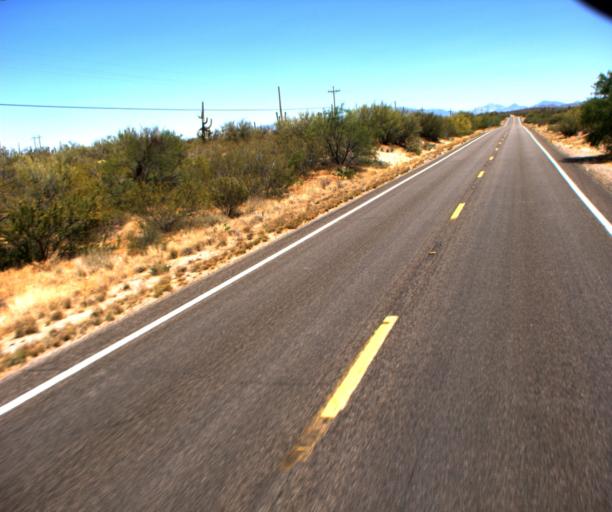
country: US
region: Arizona
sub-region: Pima County
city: Catalina
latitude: 32.7127
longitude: -111.1016
